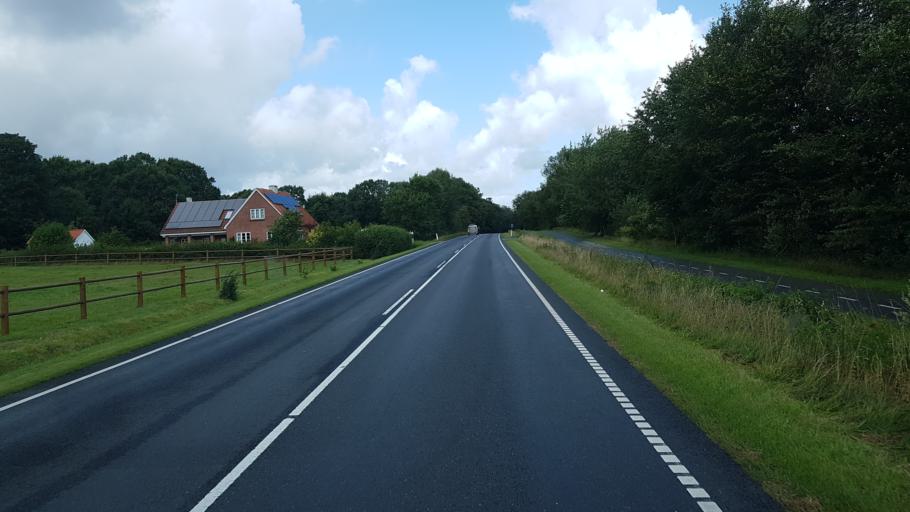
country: DK
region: South Denmark
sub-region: Vejen Kommune
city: Vejen
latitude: 55.5323
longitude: 9.1121
